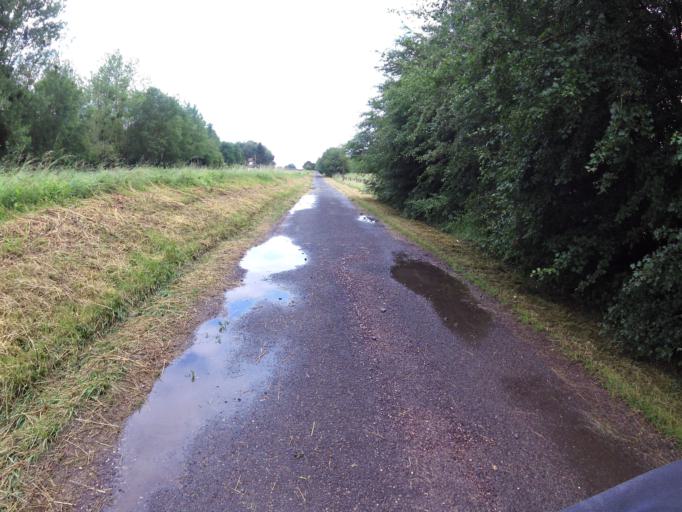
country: FR
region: Champagne-Ardenne
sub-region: Departement de la Marne
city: Sermaize-les-Bains
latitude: 48.7903
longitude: 4.9176
